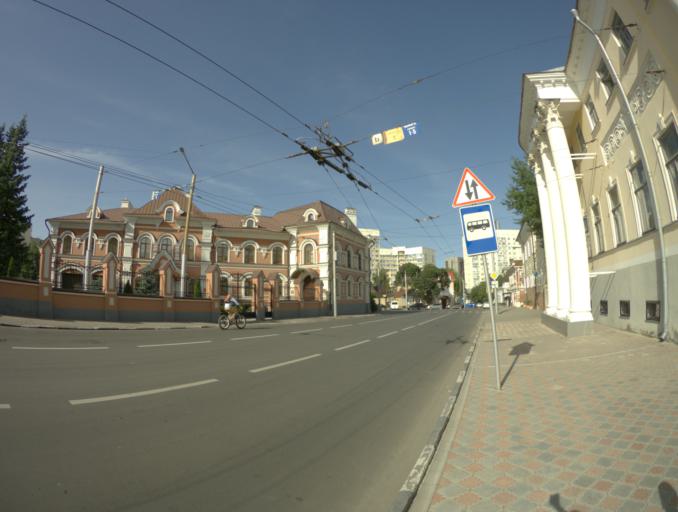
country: RU
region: Saratov
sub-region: Saratovskiy Rayon
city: Saratov
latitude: 51.5277
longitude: 46.0561
